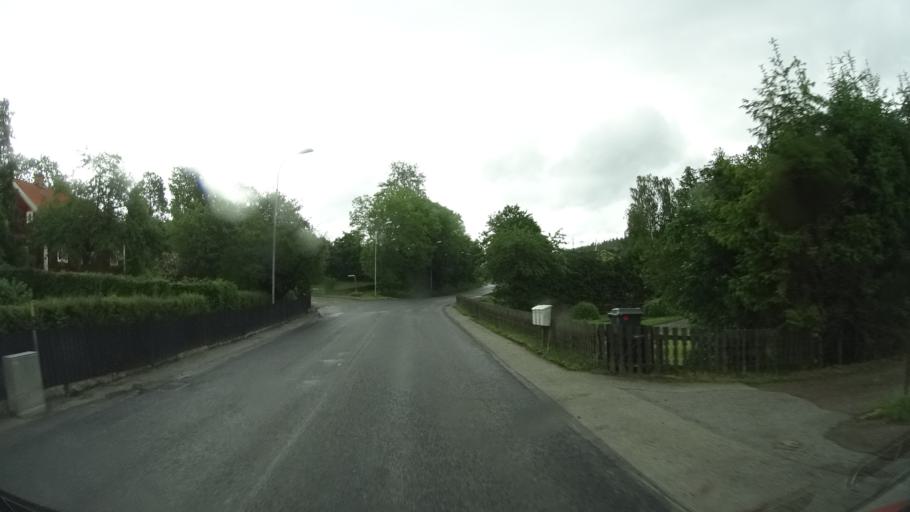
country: SE
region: Kalmar
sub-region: Oskarshamns Kommun
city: Oskarshamn
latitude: 57.3981
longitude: 16.1982
